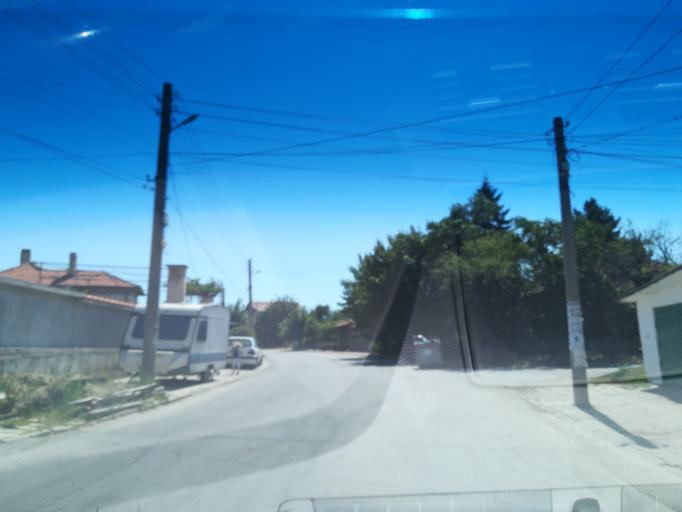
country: BG
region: Pazardzhik
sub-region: Obshtina Pazardzhik
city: Pazardzhik
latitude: 42.3345
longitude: 24.4006
